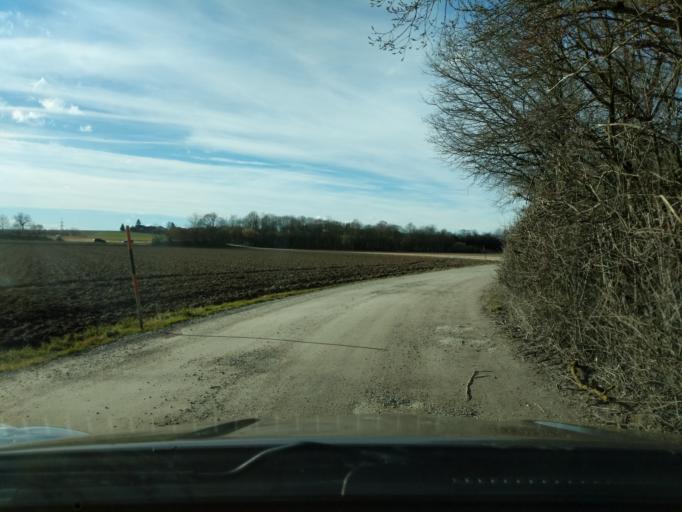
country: DE
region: Bavaria
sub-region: Upper Bavaria
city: Zorneding
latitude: 48.1023
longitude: 11.8353
